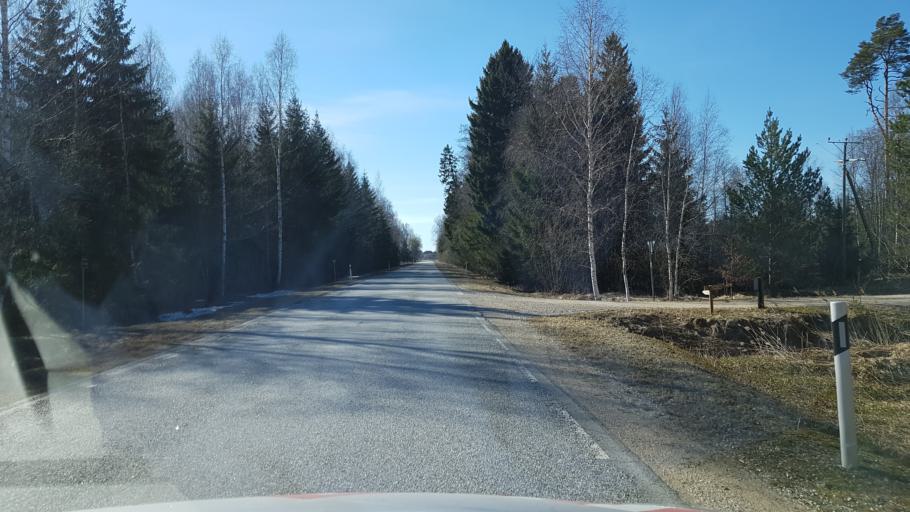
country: EE
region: Ida-Virumaa
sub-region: Kivioli linn
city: Kivioli
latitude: 59.2319
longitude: 26.7615
